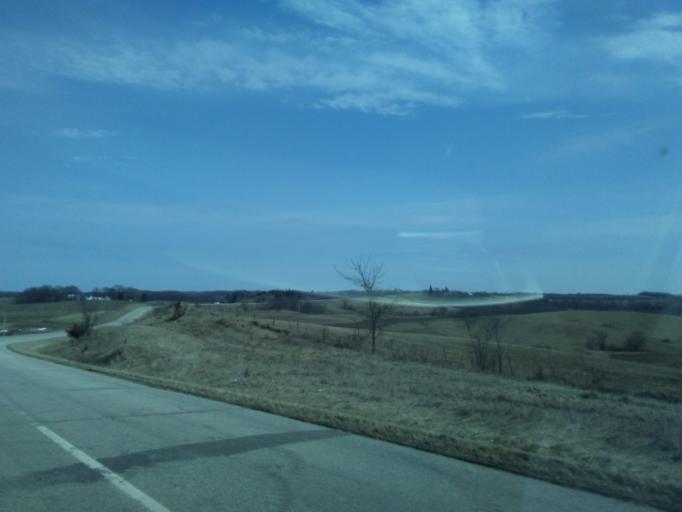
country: US
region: Wisconsin
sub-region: Crawford County
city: Prairie du Chien
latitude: 43.1394
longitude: -91.2500
